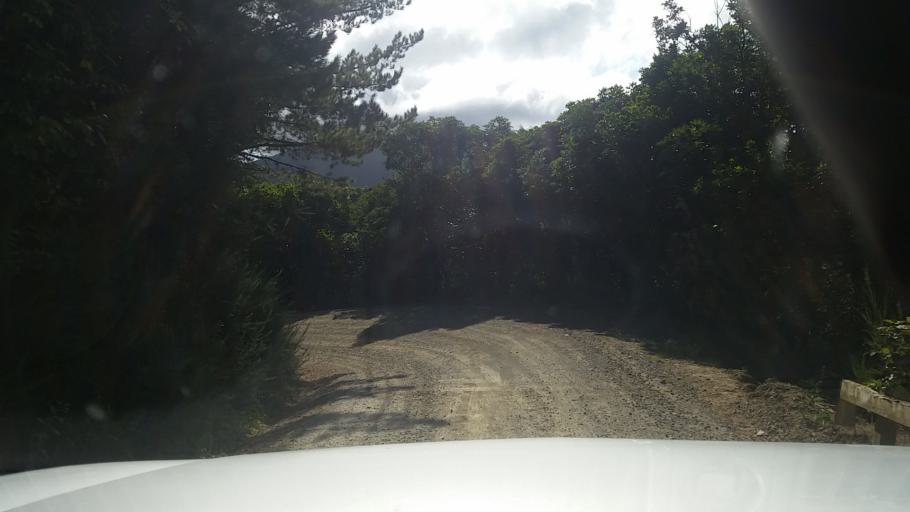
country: NZ
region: Marlborough
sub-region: Marlborough District
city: Picton
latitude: -41.2897
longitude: 174.1286
